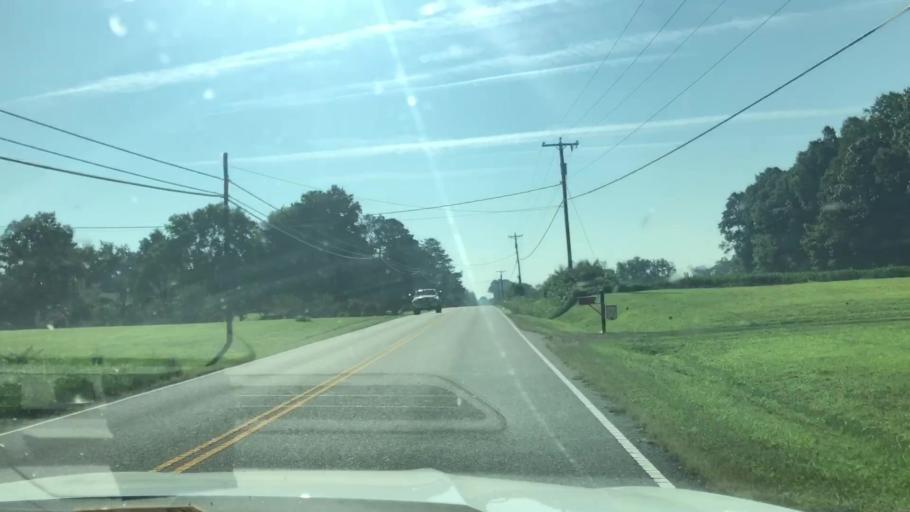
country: US
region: Virginia
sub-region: Richmond County
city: Warsaw
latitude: 37.8954
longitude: -76.6491
